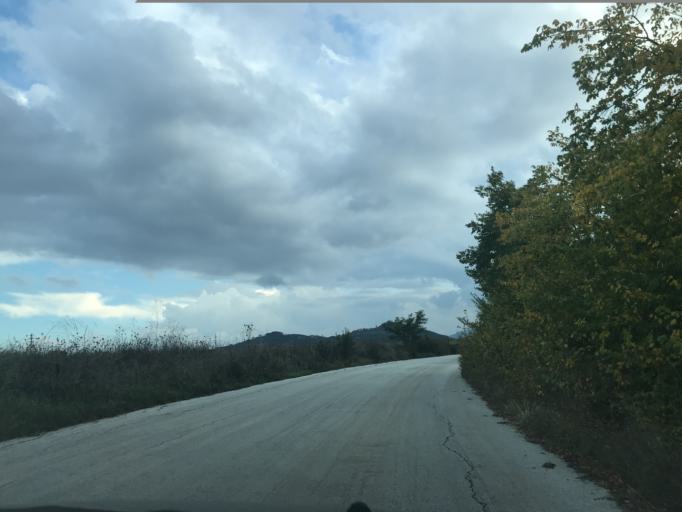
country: IT
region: Molise
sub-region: Provincia di Isernia
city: Bagnoli del Trigno
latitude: 41.6889
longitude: 14.4619
